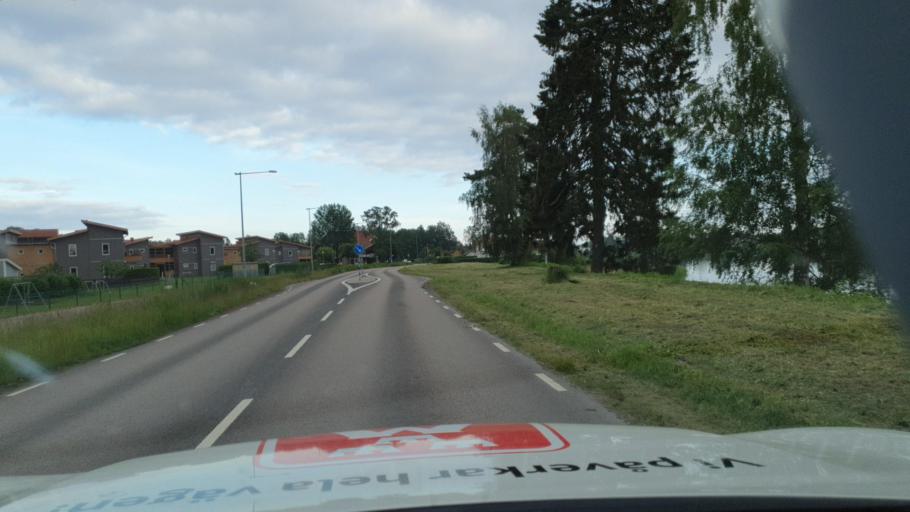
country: SE
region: Vaermland
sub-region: Karlstads Kommun
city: Karlstad
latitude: 59.4155
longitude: 13.4911
